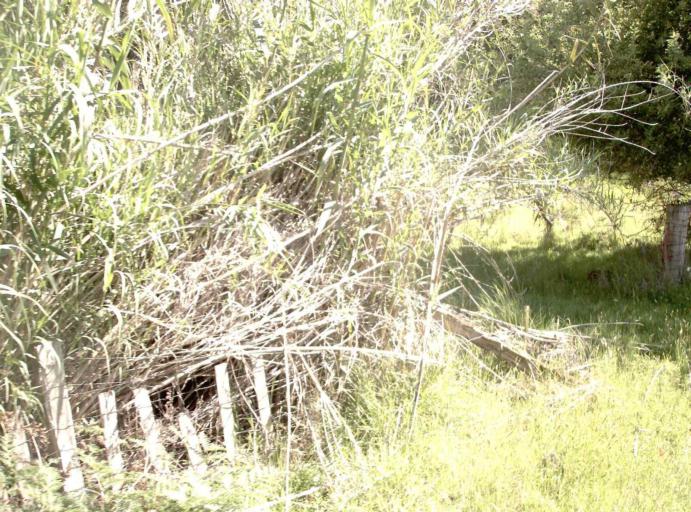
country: AU
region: New South Wales
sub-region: Bombala
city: Bombala
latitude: -37.3444
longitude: 148.6944
